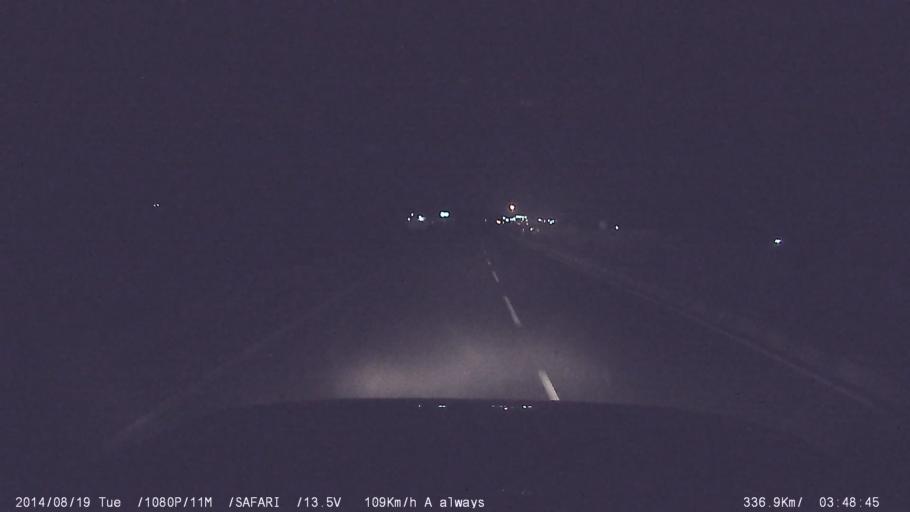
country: IN
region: Tamil Nadu
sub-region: Erode
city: Vijayapuri
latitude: 11.2408
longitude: 77.5113
